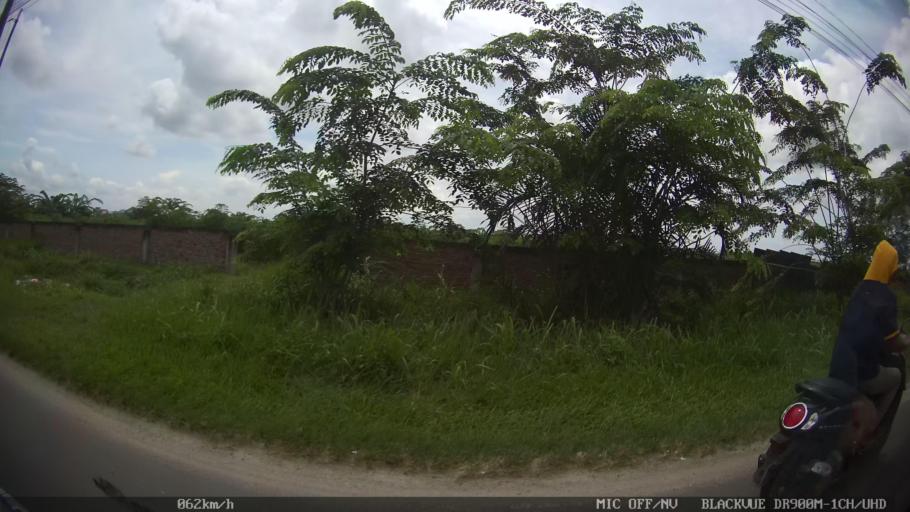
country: ID
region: North Sumatra
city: Percut
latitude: 3.5756
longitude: 98.8832
